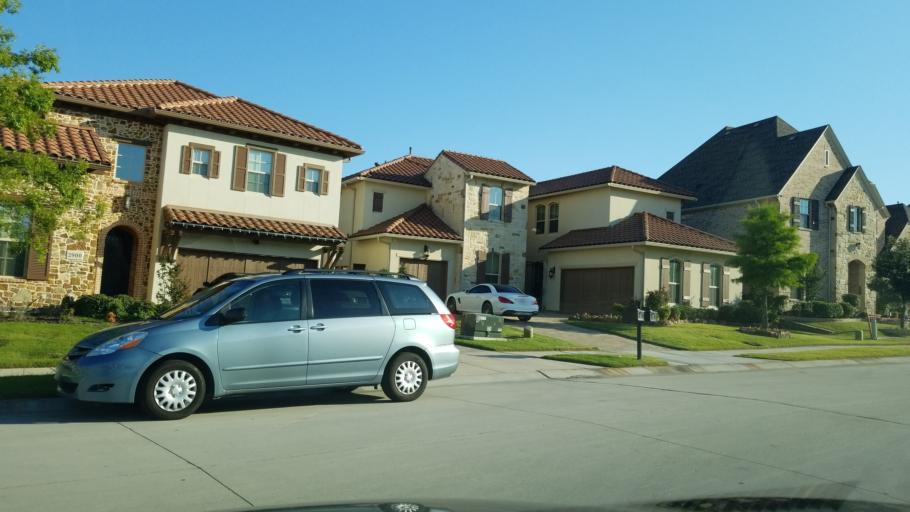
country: US
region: Texas
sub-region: Dallas County
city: Coppell
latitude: 32.9068
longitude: -96.9863
